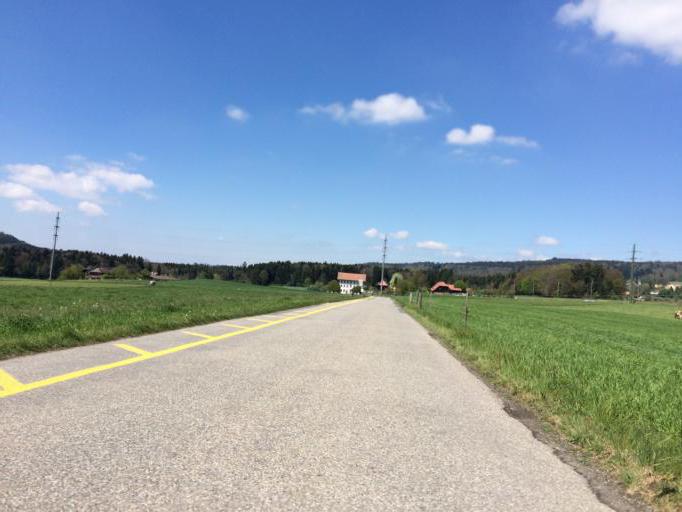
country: CH
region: Bern
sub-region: Bern-Mittelland District
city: Rubigen
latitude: 46.9187
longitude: 7.5449
